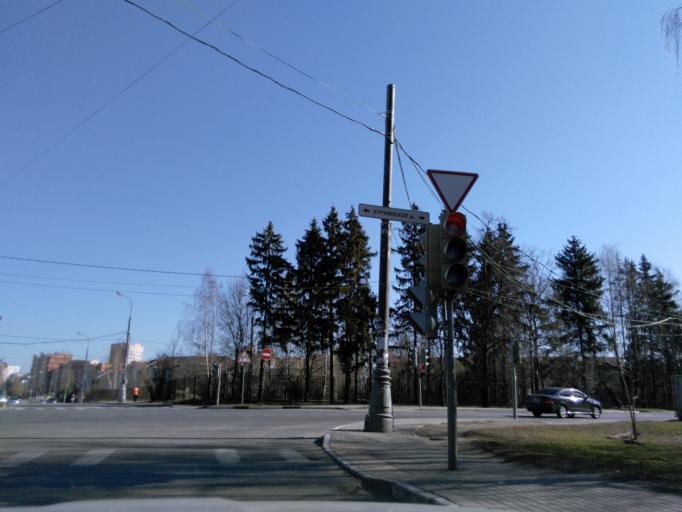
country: RU
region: Moscow
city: Khimki
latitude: 55.8855
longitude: 37.3926
